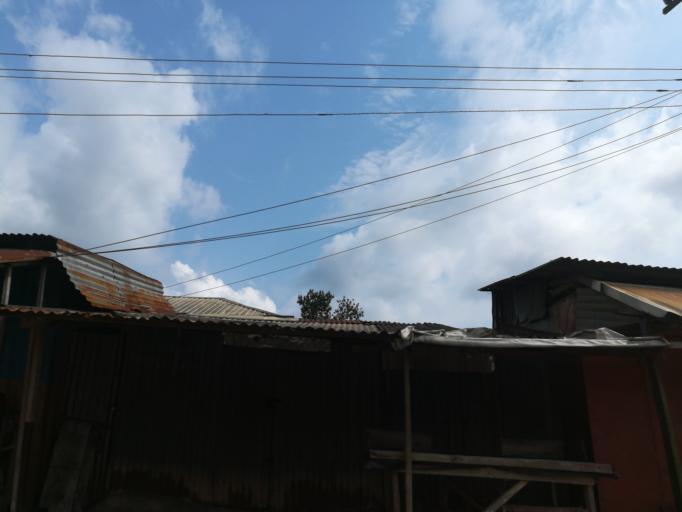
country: NG
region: Rivers
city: Okrika
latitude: 4.7492
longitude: 7.1068
